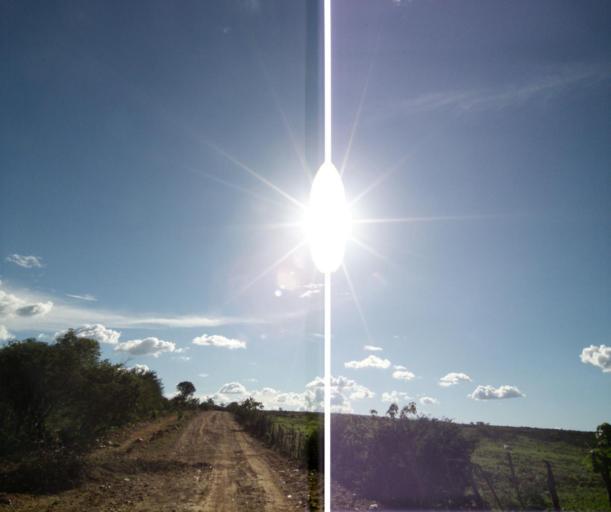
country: BR
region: Bahia
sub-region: Tanhacu
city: Tanhacu
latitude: -14.1832
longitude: -40.9328
